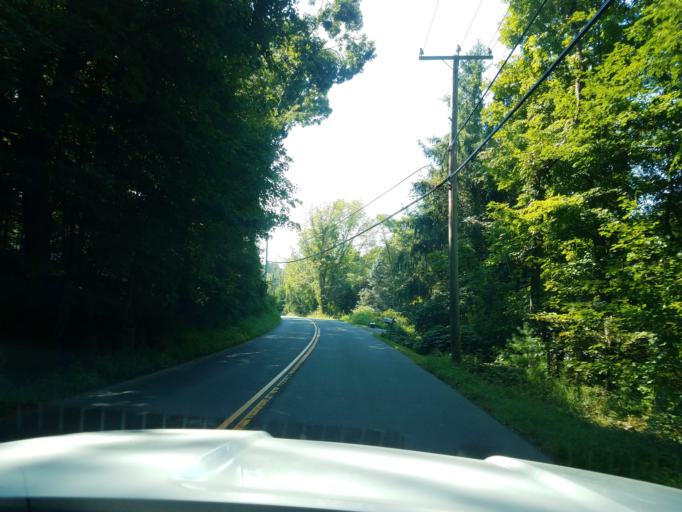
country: US
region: Connecticut
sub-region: Fairfield County
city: Newtown
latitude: 41.3650
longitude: -73.3375
